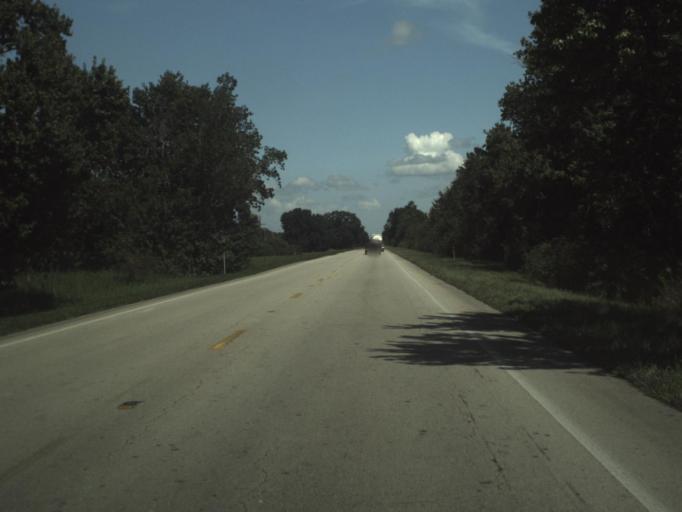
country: US
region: Florida
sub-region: Martin County
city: Indiantown
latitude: 27.0026
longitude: -80.4410
